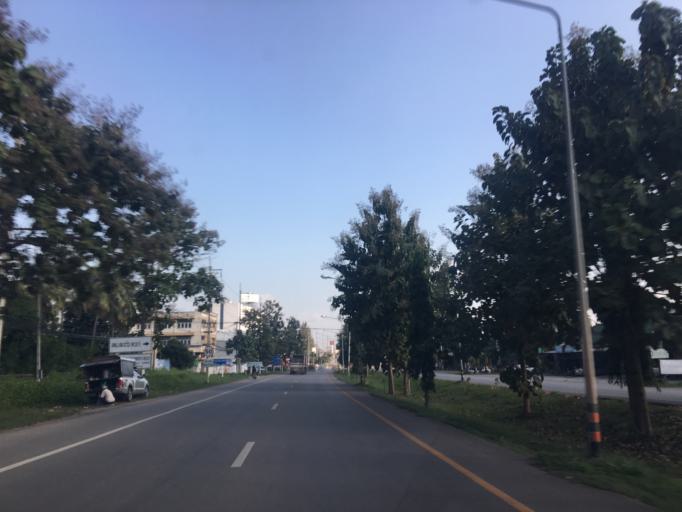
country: TH
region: Phayao
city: Phayao
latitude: 19.1801
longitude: 99.8989
